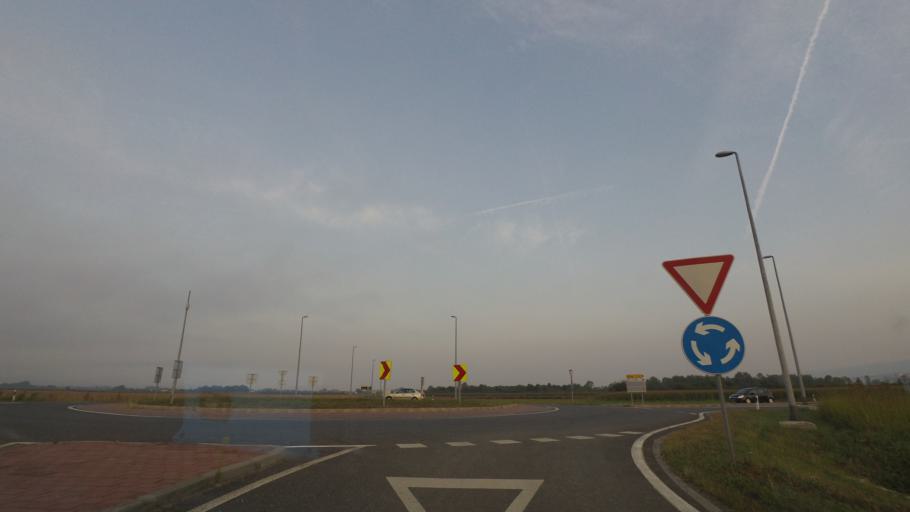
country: HR
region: Brodsko-Posavska
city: Ljupina
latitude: 45.2352
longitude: 17.4117
